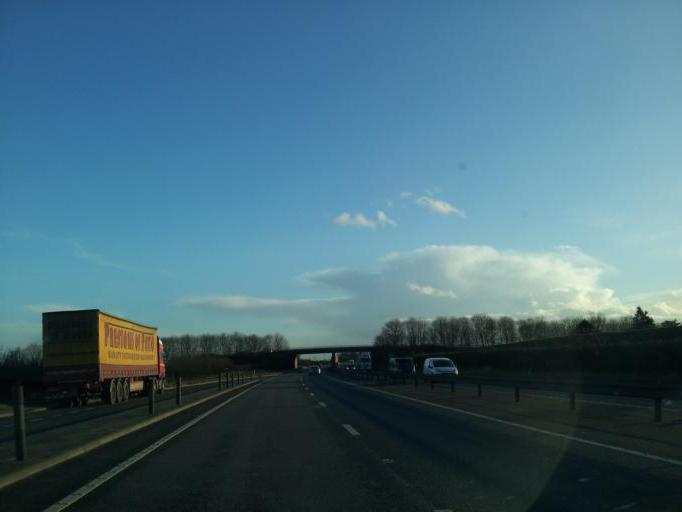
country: GB
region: England
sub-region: Nottinghamshire
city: Newark on Trent
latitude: 53.0661
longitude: -0.7654
